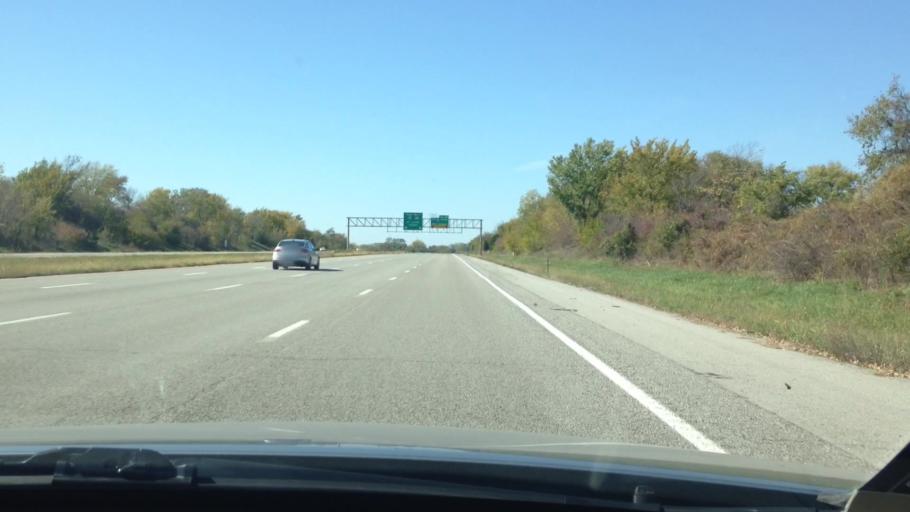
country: US
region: Missouri
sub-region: Platte County
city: Weatherby Lake
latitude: 39.3077
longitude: -94.6560
